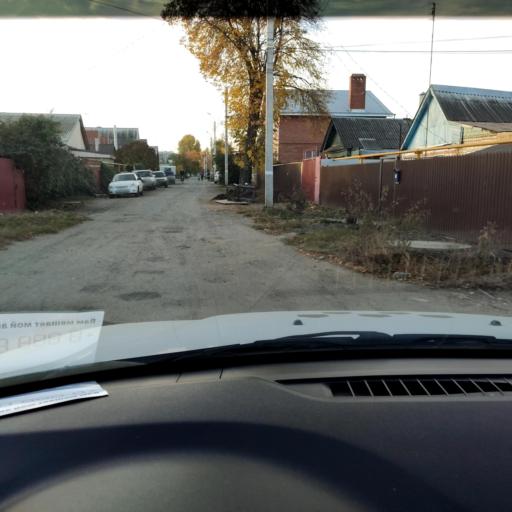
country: RU
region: Samara
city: Tol'yatti
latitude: 53.5359
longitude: 49.4250
